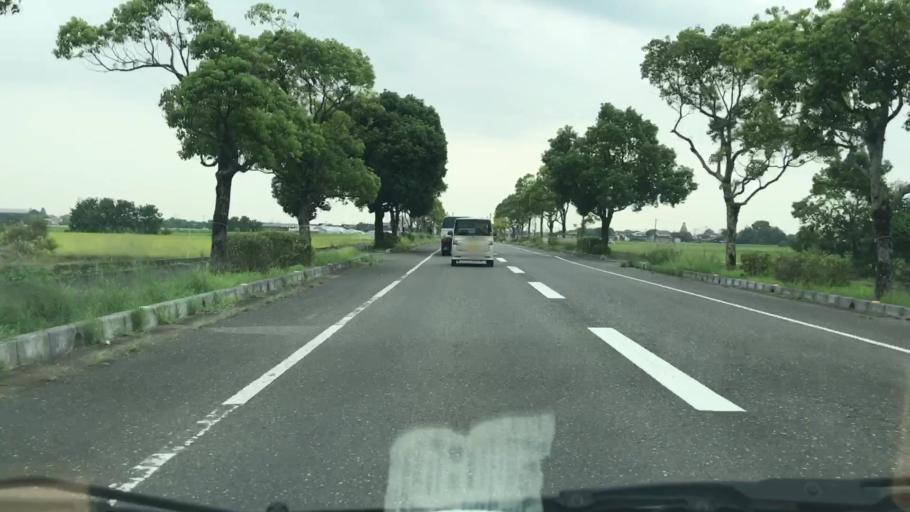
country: JP
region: Saga Prefecture
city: Saga-shi
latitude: 33.2307
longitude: 130.3060
